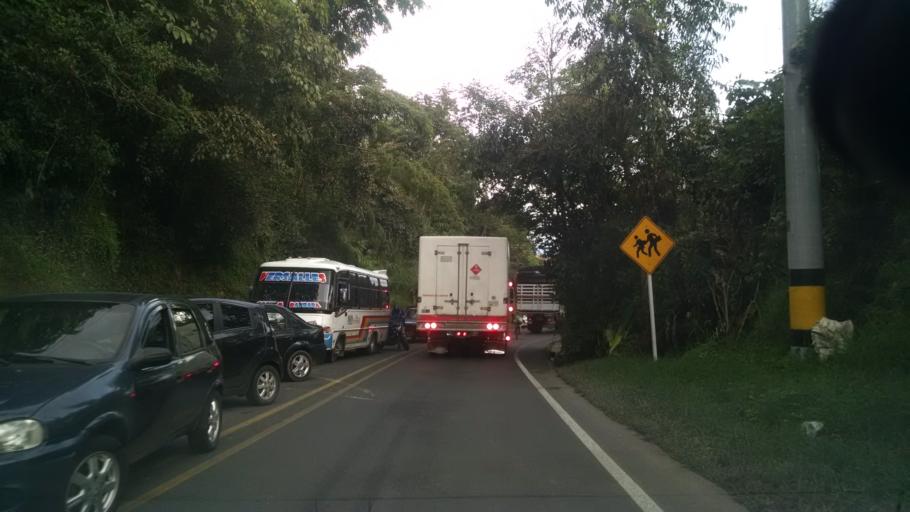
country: CO
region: Antioquia
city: Santa Barbara
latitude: 5.8840
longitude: -75.5719
